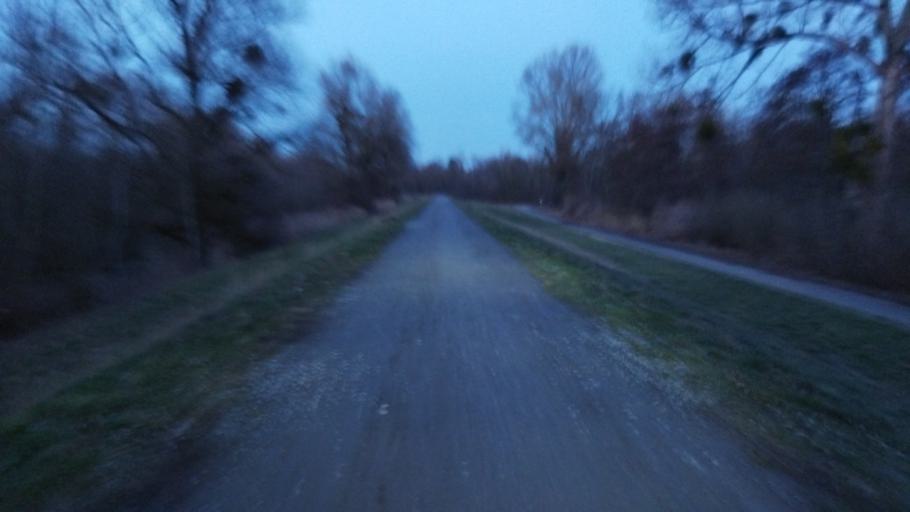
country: DE
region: Baden-Wuerttemberg
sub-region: Karlsruhe Region
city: Eggenstein-Leopoldshafen
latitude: 49.0870
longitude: 8.3602
